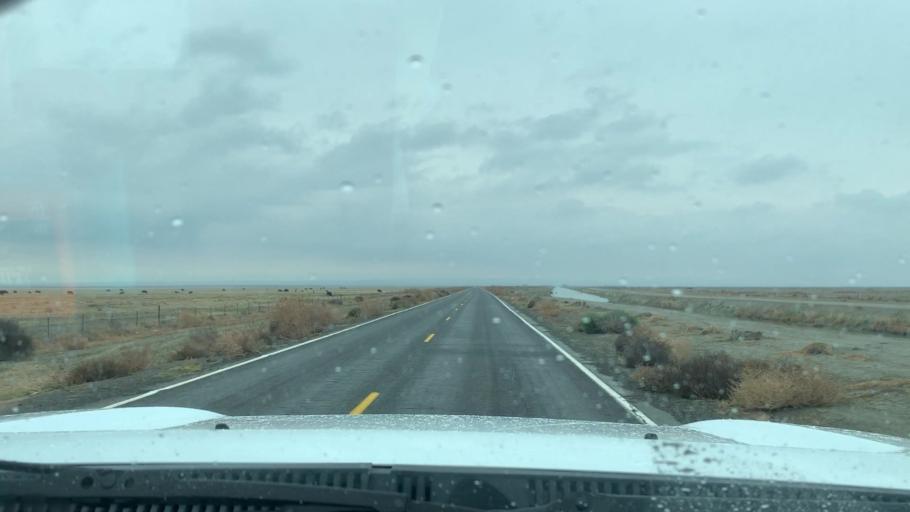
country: US
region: California
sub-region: Kings County
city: Kettleman City
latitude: 35.9340
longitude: -119.7613
